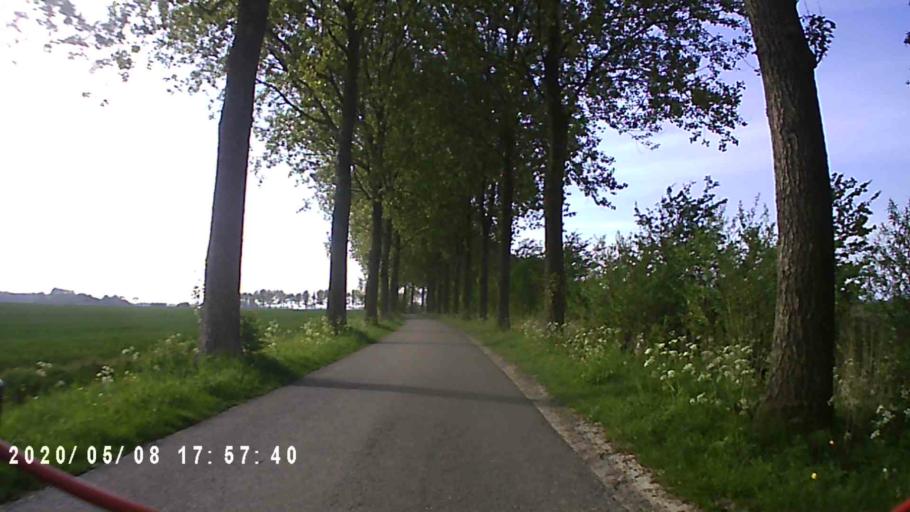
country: NL
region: Groningen
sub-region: Gemeente Winsum
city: Winsum
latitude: 53.3681
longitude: 6.4859
